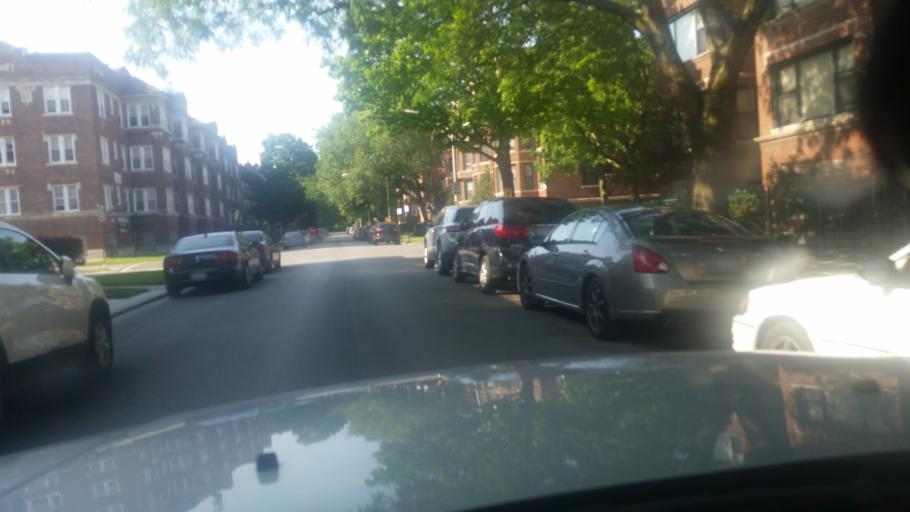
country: US
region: Illinois
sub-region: Cook County
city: Chicago
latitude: 41.7713
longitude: -87.5728
